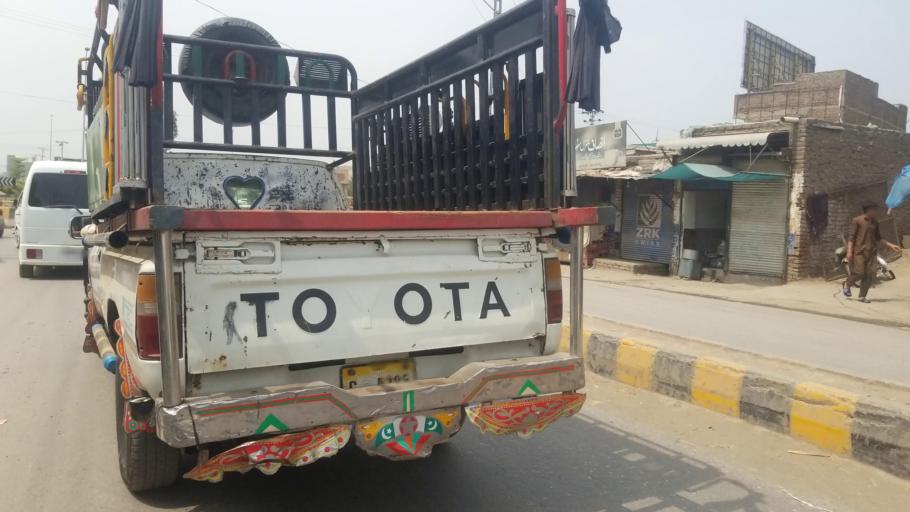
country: PK
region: Khyber Pakhtunkhwa
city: Peshawar
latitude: 33.9968
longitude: 71.6068
